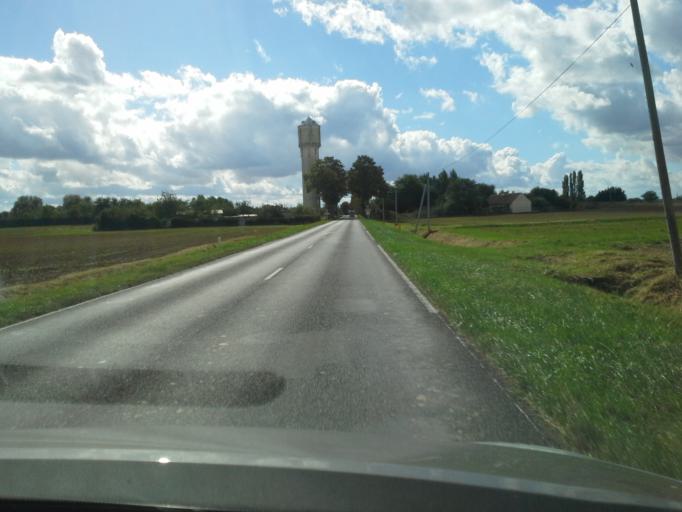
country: FR
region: Centre
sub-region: Departement du Loir-et-Cher
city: Pontlevoy
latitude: 47.4004
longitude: 1.2630
